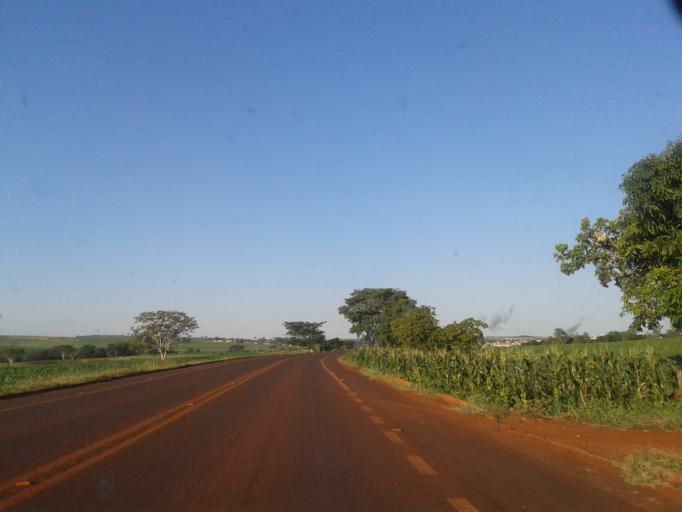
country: BR
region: Minas Gerais
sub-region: Capinopolis
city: Capinopolis
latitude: -18.6843
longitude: -49.5982
